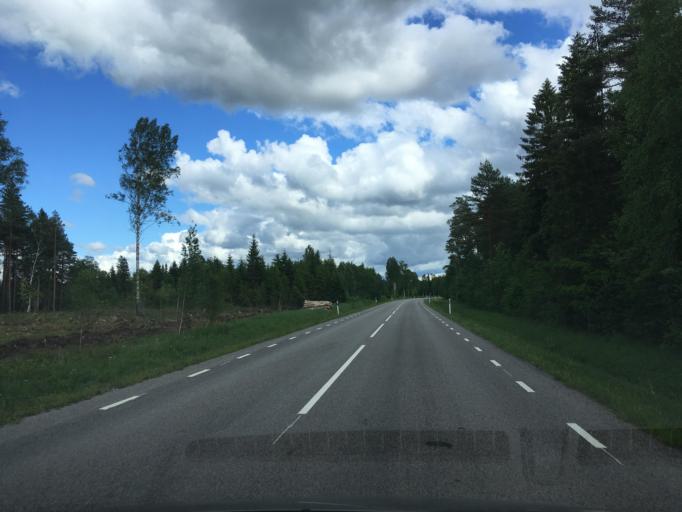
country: EE
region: Paernumaa
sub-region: Tootsi vald
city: Tootsi
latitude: 58.6613
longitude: 24.6764
